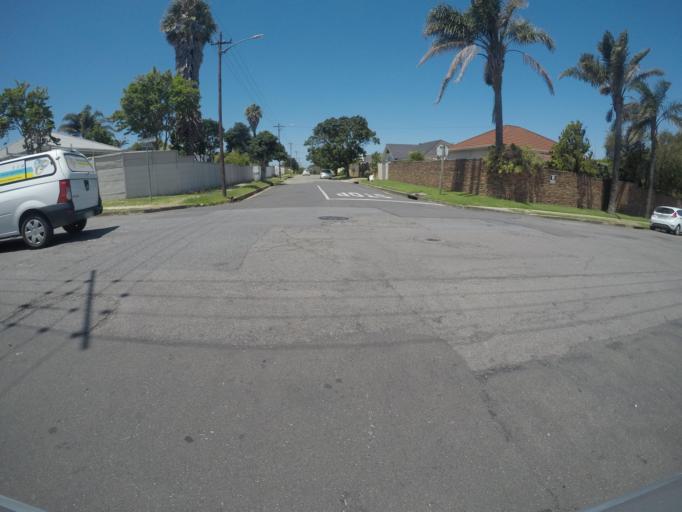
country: ZA
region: Eastern Cape
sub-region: Buffalo City Metropolitan Municipality
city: East London
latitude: -32.9887
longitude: 27.9063
